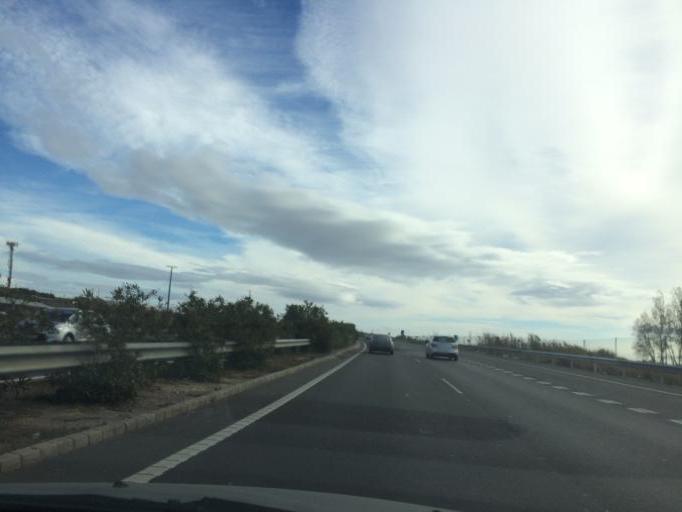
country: ES
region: Andalusia
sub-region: Provincia de Almeria
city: Viator
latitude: 36.8437
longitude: -2.4042
